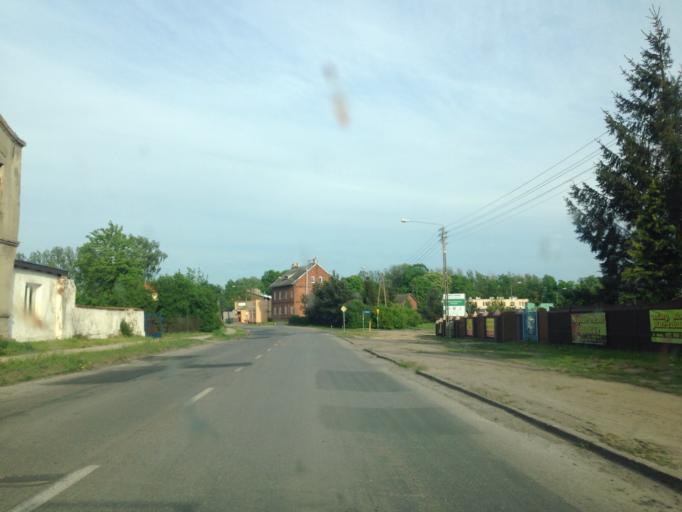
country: PL
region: Kujawsko-Pomorskie
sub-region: Powiat wabrzeski
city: Wabrzezno
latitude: 53.2674
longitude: 18.9794
